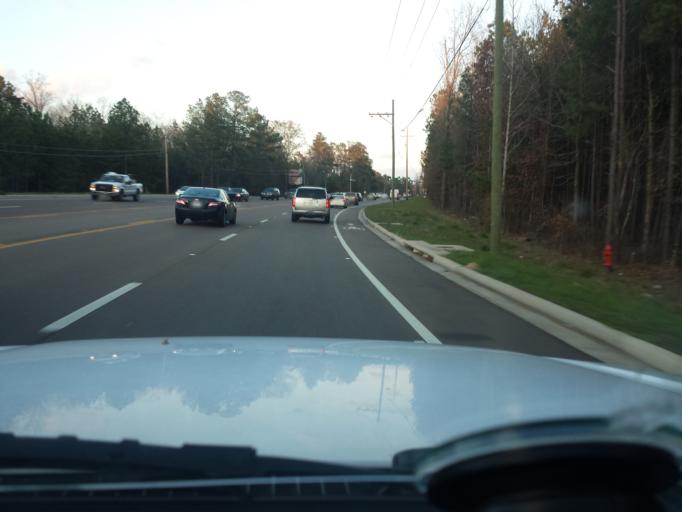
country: US
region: Mississippi
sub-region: Madison County
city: Ridgeland
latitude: 32.3696
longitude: -90.0535
